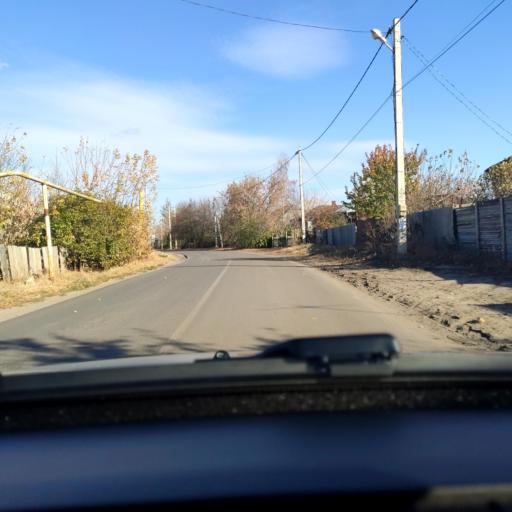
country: RU
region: Voronezj
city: Shilovo
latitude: 51.5232
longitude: 39.1485
